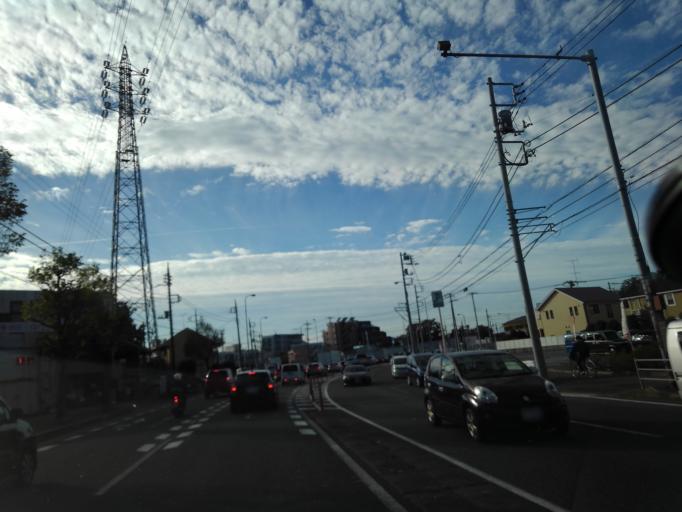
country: JP
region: Tokyo
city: Fussa
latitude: 35.7255
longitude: 139.3434
